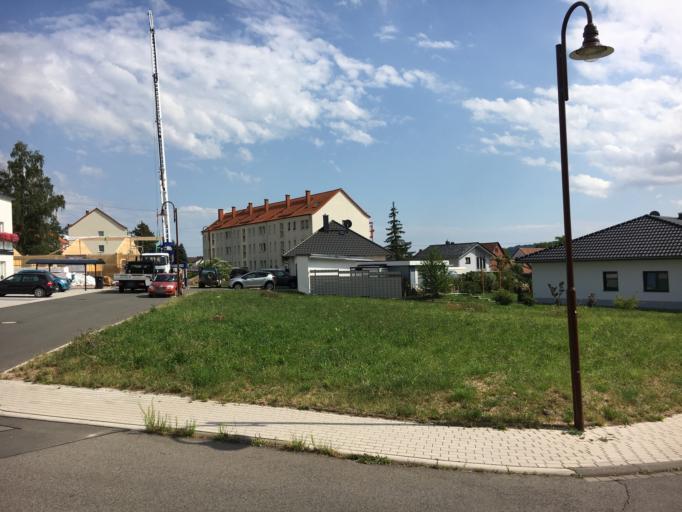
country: DE
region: Thuringia
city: Breitungen
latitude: 50.7638
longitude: 10.3302
